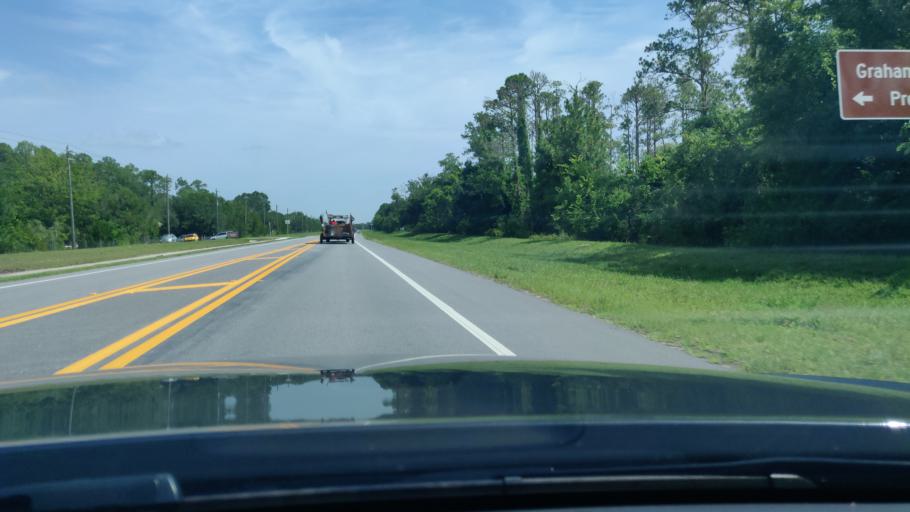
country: US
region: Florida
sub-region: Flagler County
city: Flagler Beach
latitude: 29.5072
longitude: -81.1607
